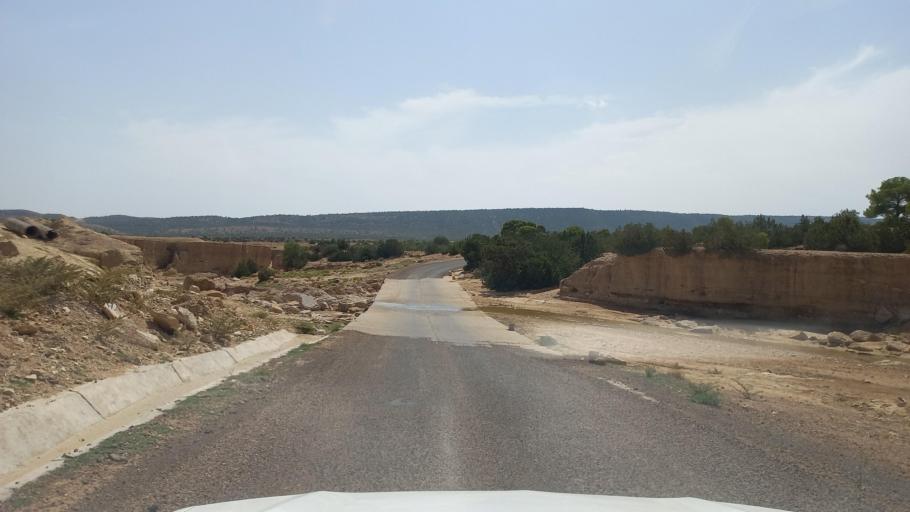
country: TN
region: Al Qasrayn
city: Sbiba
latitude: 35.3976
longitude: 8.9486
